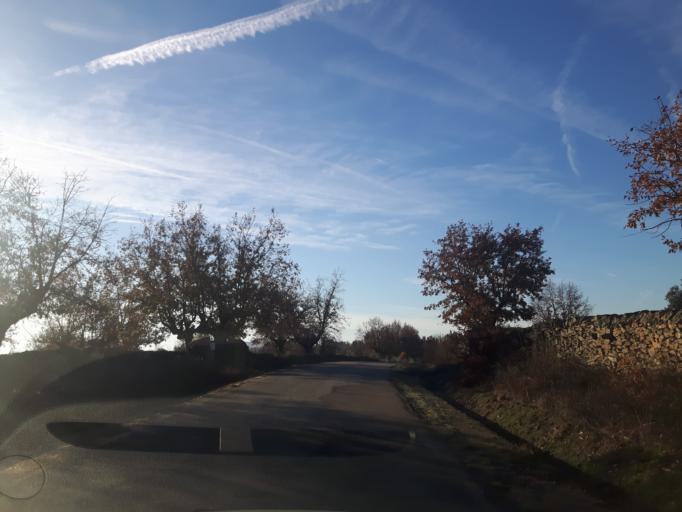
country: ES
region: Castille and Leon
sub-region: Provincia de Salamanca
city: Cerralbo
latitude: 40.9408
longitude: -6.6191
